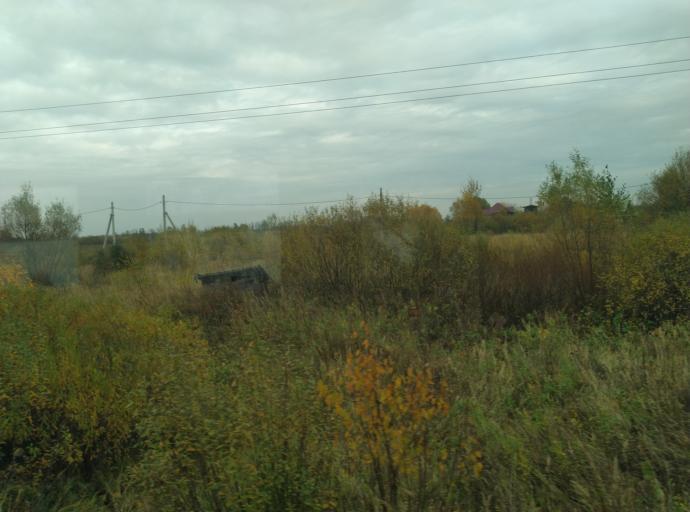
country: RU
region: Moskovskaya
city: Bol'shiye Vyazemy
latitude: 55.6314
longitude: 36.9750
